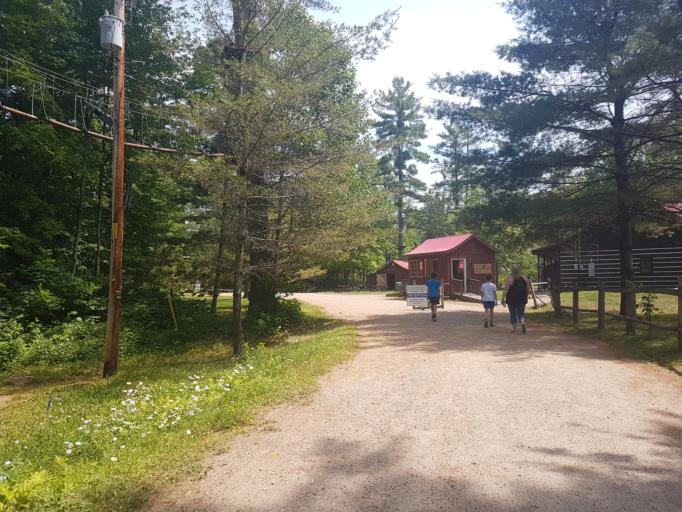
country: CA
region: Quebec
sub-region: Outaouais
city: Fort-Coulonge
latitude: 45.8756
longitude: -76.6877
